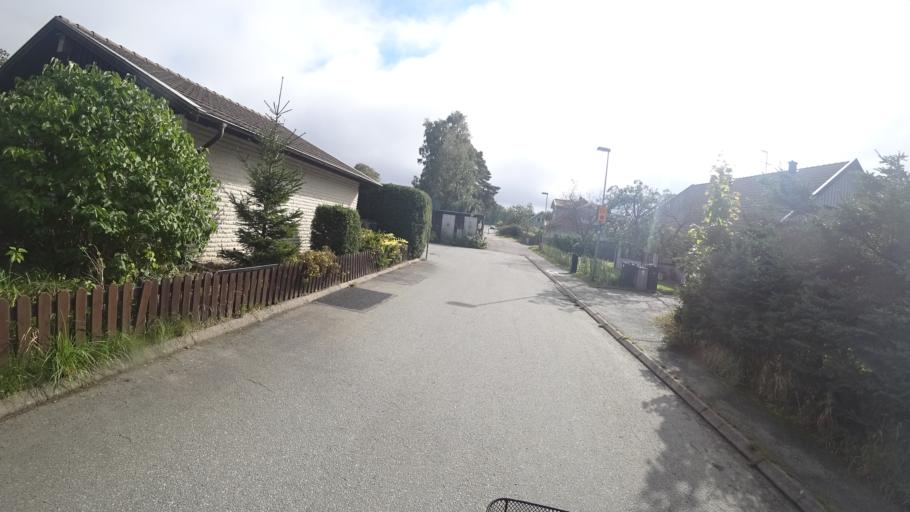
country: SE
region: Vaestra Goetaland
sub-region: Molndal
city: Moelndal
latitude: 57.6318
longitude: 11.9537
